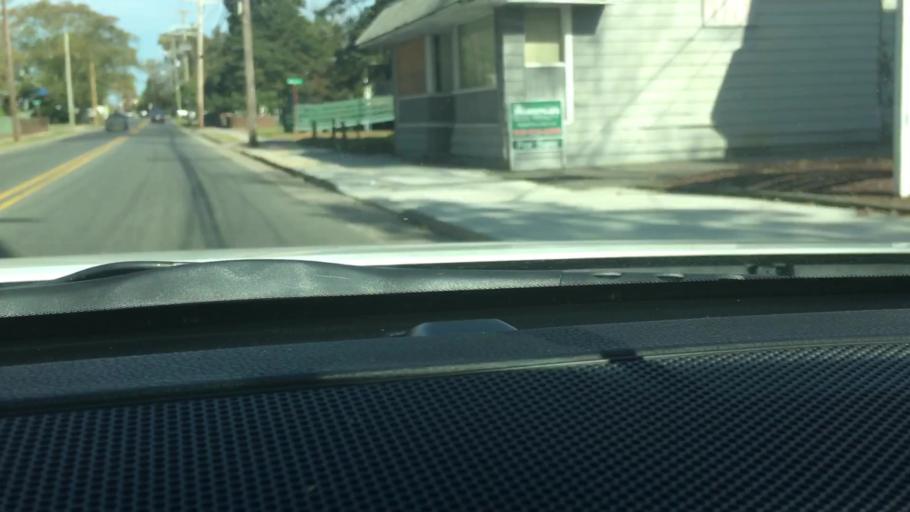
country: US
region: New Jersey
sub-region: Atlantic County
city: Pleasantville
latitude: 39.3800
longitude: -74.5334
